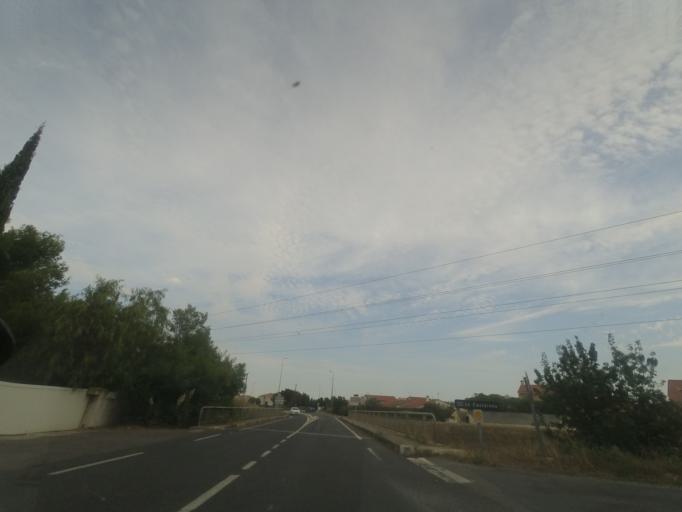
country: FR
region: Languedoc-Roussillon
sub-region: Departement des Pyrenees-Orientales
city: Pezilla-la-Riviere
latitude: 42.6801
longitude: 2.7752
